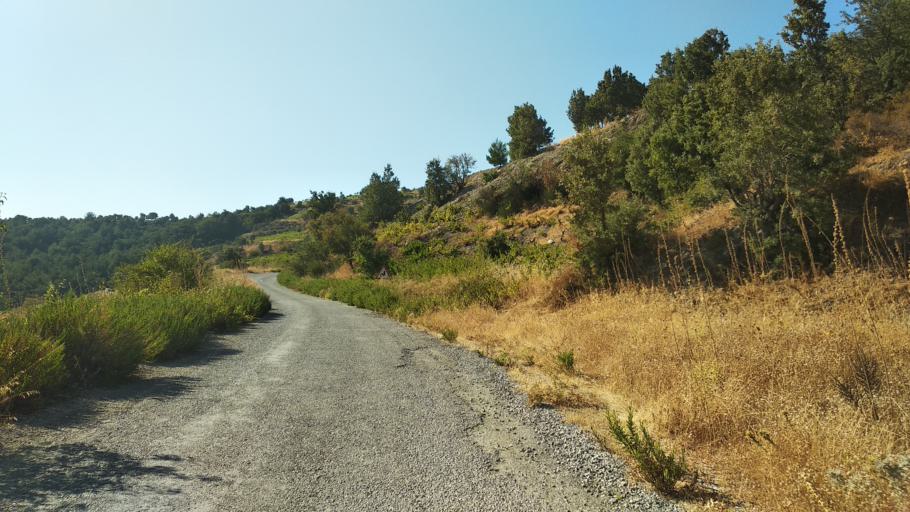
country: TR
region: Izmir
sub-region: Seferihisar
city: Seferhisar
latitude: 38.3286
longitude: 26.9495
